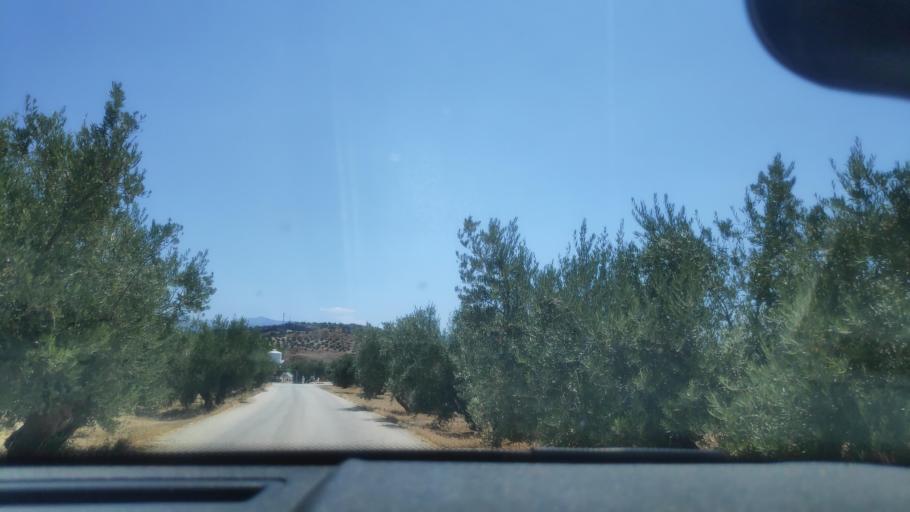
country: ES
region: Andalusia
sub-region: Provincia de Jaen
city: Jaen
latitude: 37.8284
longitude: -3.7591
